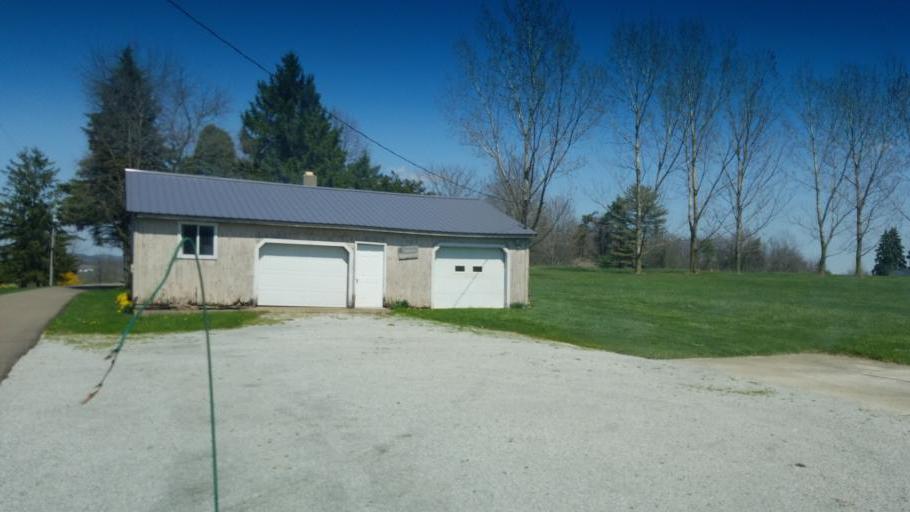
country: US
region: Ohio
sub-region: Stark County
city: Brewster
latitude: 40.6945
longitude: -81.6990
